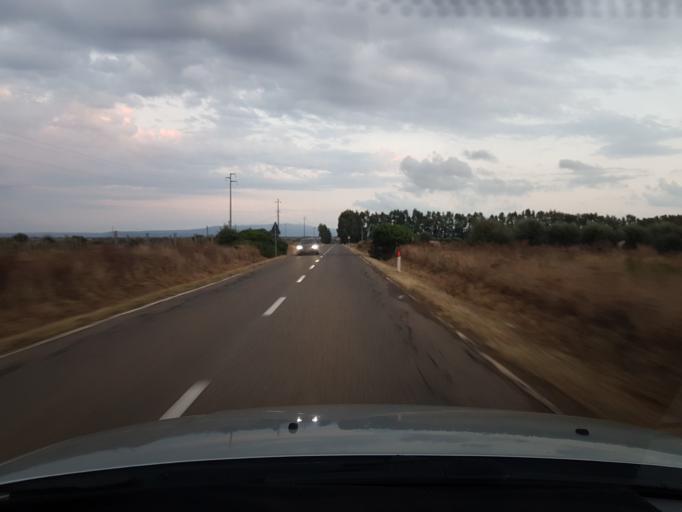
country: IT
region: Sardinia
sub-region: Provincia di Oristano
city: Tramatza
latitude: 40.0236
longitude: 8.6417
